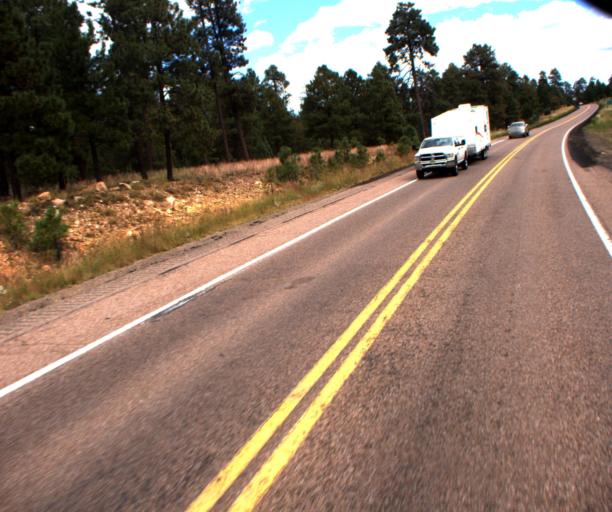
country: US
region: Arizona
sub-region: Navajo County
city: Heber-Overgaard
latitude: 34.3505
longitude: -110.7030
